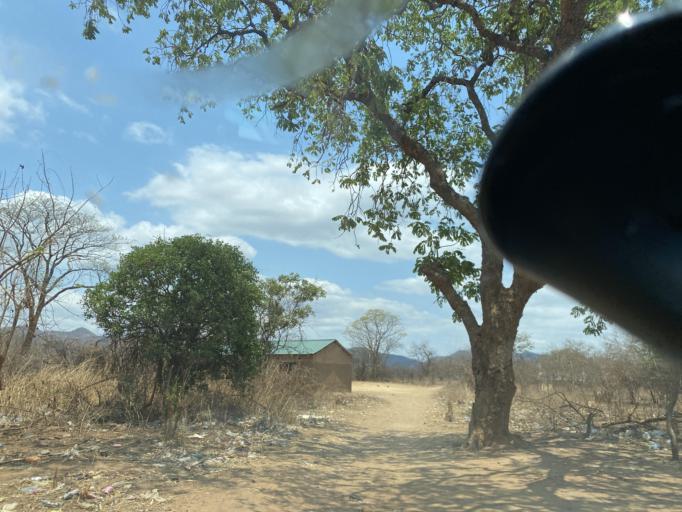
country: ZM
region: Lusaka
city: Luangwa
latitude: -15.1868
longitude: 29.7303
